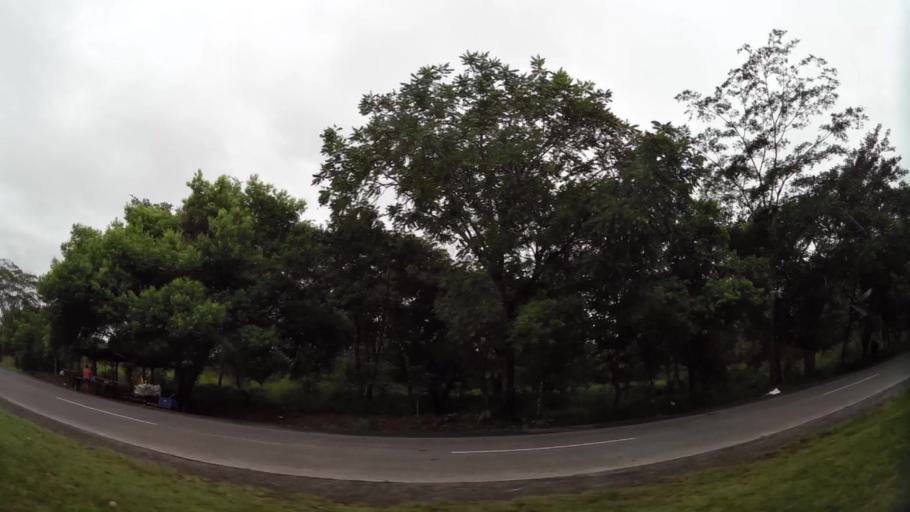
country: PA
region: Chiriqui
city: La Concepcion
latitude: 8.5005
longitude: -82.5999
